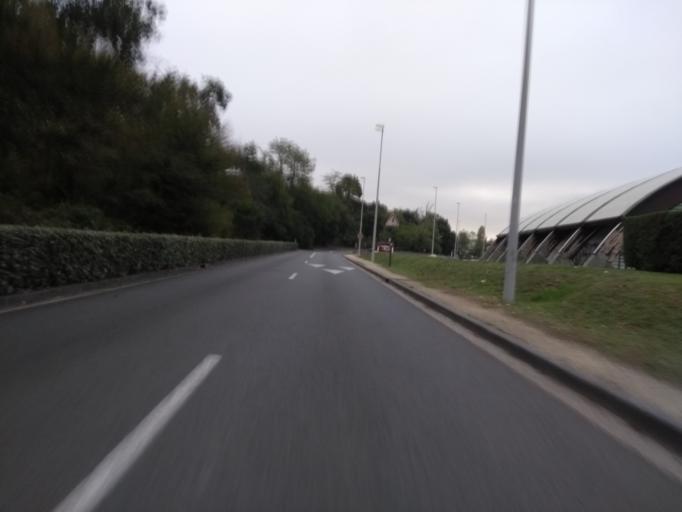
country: FR
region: Aquitaine
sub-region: Departement de la Gironde
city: Talence
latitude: 44.7938
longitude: -0.5978
